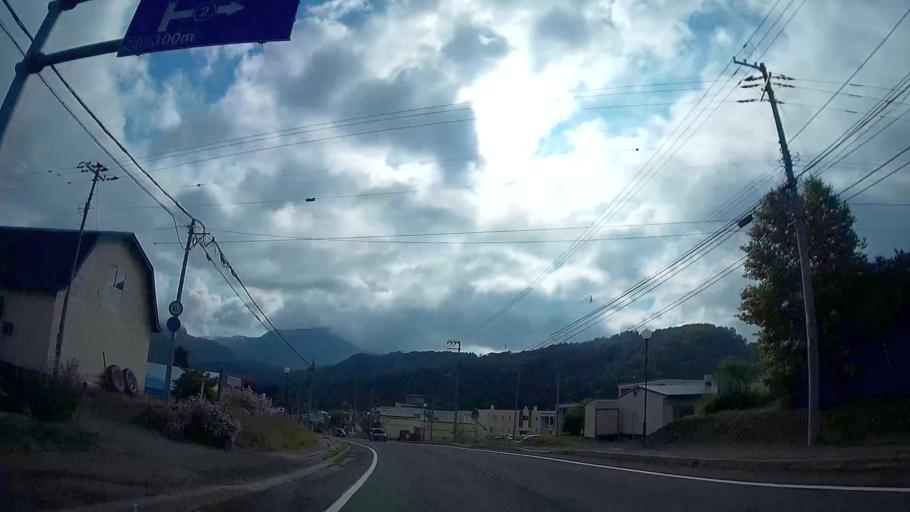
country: JP
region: Hokkaido
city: Date
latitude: 42.5588
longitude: 140.8913
